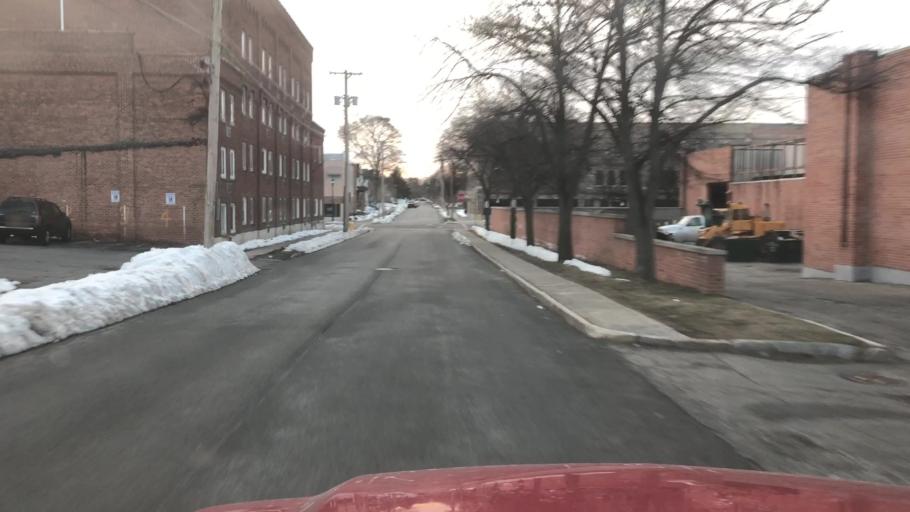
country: US
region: New York
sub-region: Monroe County
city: East Rochester
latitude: 43.1119
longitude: -77.4845
